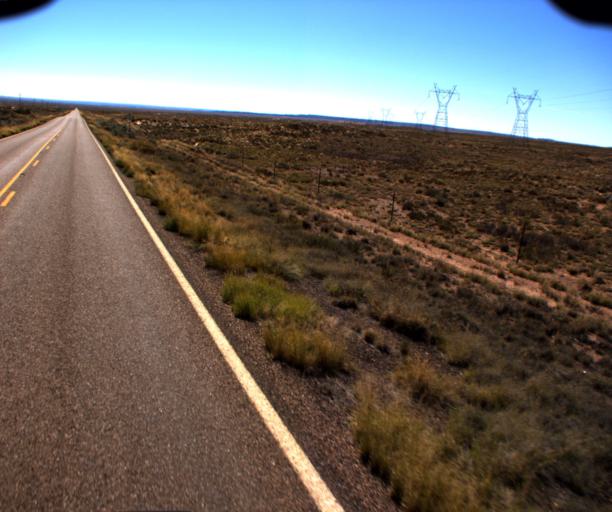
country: US
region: Arizona
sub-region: Navajo County
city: Holbrook
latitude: 35.1603
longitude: -110.0820
